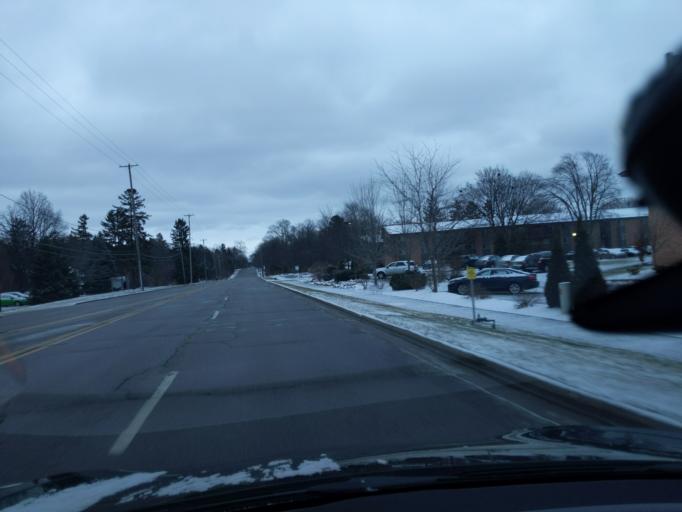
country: US
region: Michigan
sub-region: Ingham County
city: Okemos
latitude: 42.7118
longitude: -84.4602
